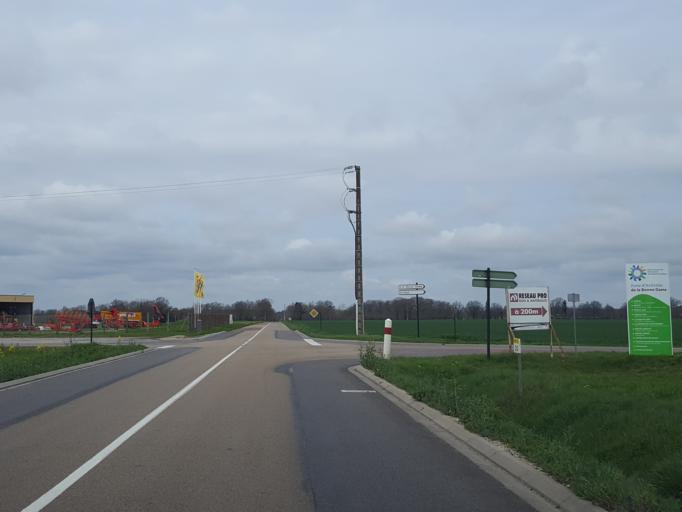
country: FR
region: Centre
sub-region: Departement du Loiret
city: Chatillon-Coligny
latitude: 47.8200
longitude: 2.8317
